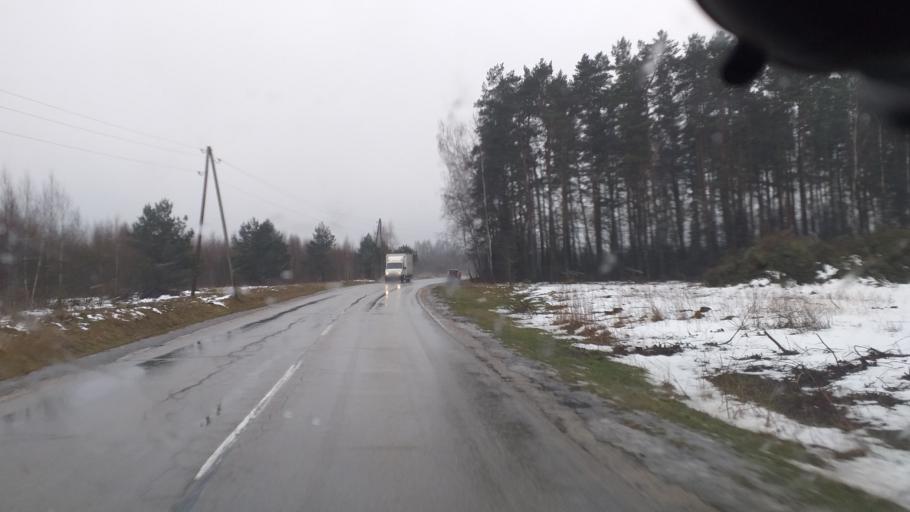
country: LV
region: Babite
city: Pinki
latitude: 56.9719
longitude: 23.9695
